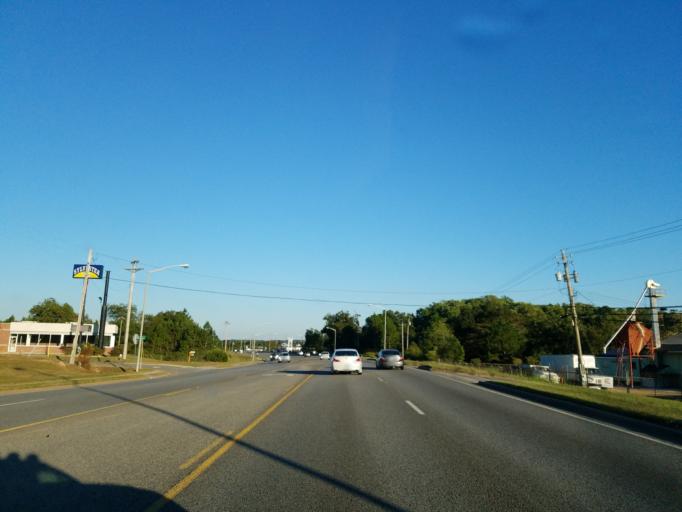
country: US
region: Georgia
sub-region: Worth County
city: Sylvester
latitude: 31.5280
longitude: -83.8202
